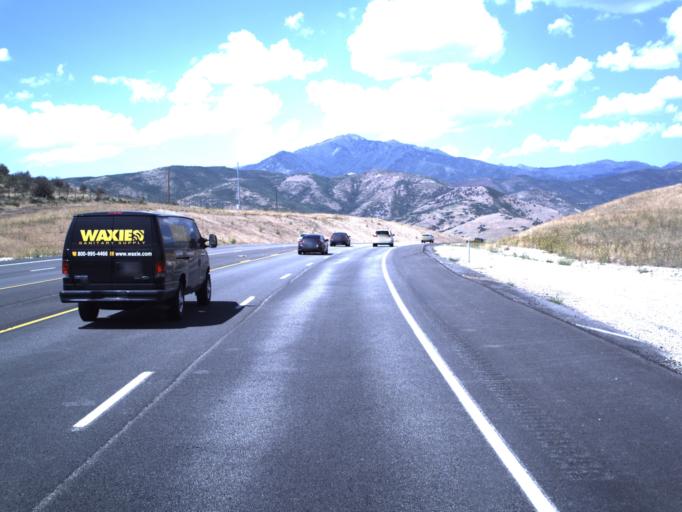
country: US
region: Utah
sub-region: Wasatch County
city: Midway
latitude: 40.4169
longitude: -111.4871
